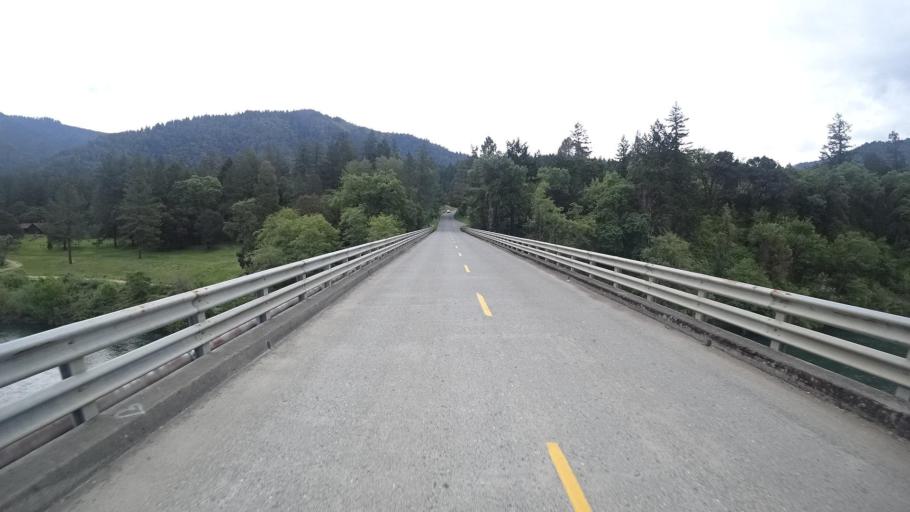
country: US
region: California
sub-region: Humboldt County
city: Willow Creek
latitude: 40.9459
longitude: -123.6244
